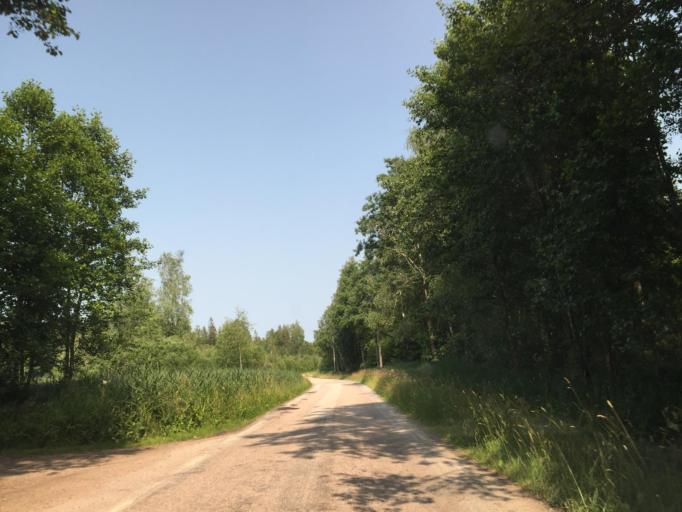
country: SE
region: Vaestra Goetaland
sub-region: Trollhattan
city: Sjuntorp
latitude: 58.2890
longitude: 12.1313
